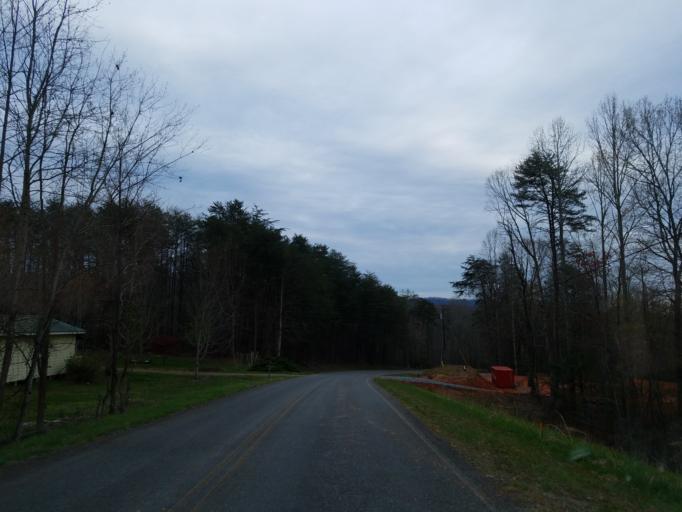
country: US
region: Georgia
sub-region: Fannin County
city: Blue Ridge
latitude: 34.7060
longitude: -84.2941
